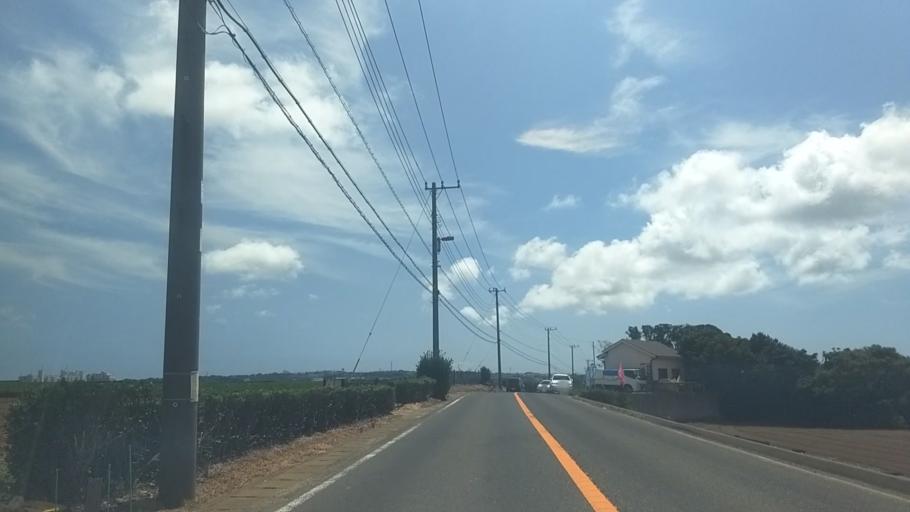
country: JP
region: Kanagawa
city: Miura
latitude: 35.1959
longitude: 139.6499
